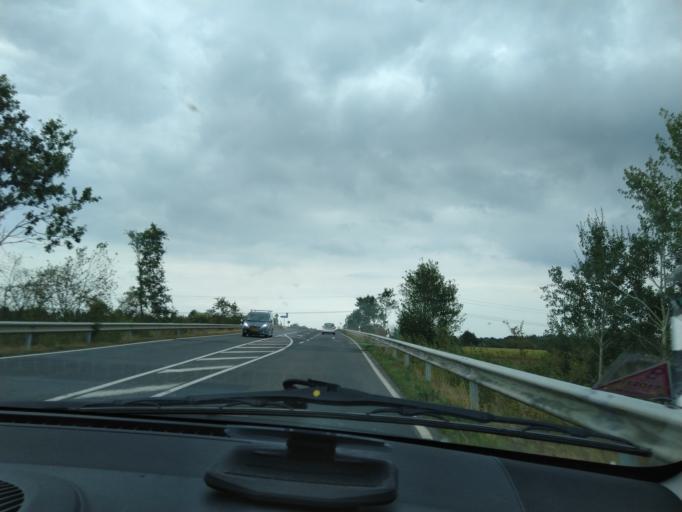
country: DE
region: Lower Saxony
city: Rhede
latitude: 53.0661
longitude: 7.2349
